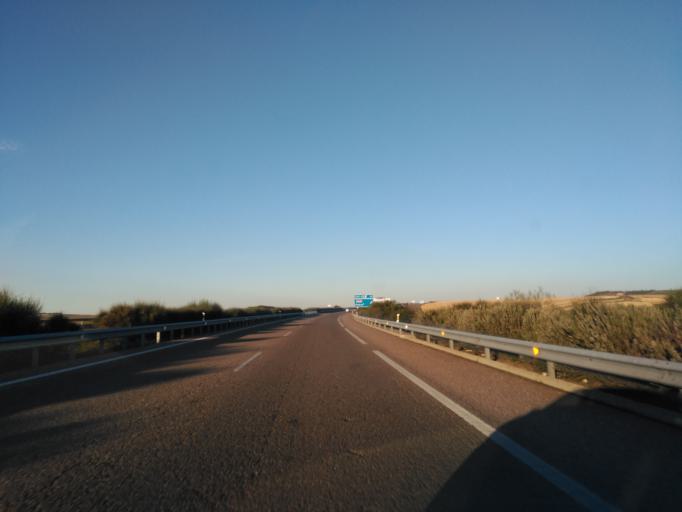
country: ES
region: Castille and Leon
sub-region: Provincia de Valladolid
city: Alaejos
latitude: 41.3147
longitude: -5.2203
